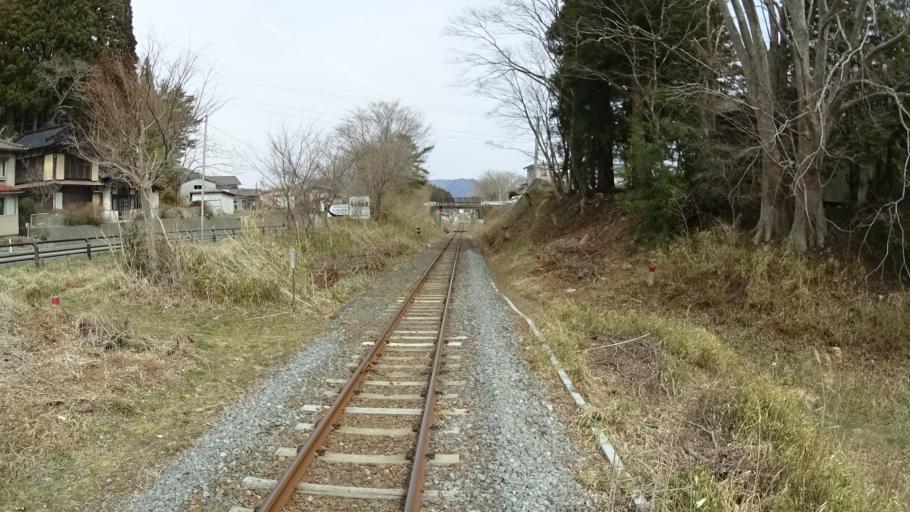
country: JP
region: Iwate
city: Yamada
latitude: 39.4285
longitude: 141.9730
